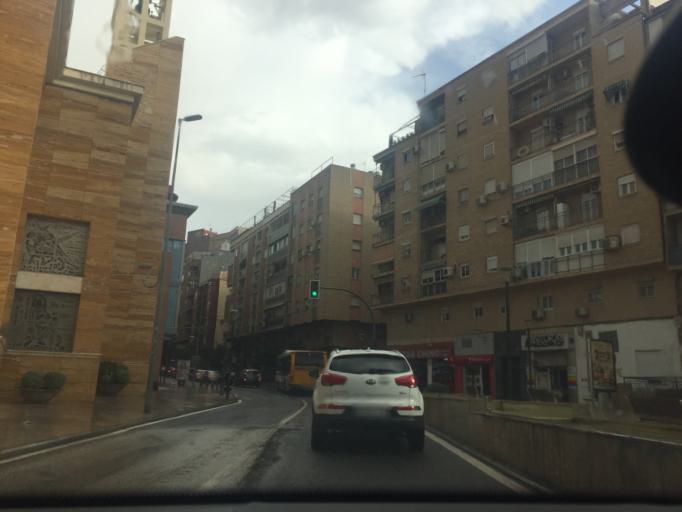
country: ES
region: Andalusia
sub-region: Provincia de Jaen
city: Jaen
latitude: 37.7784
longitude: -3.7930
